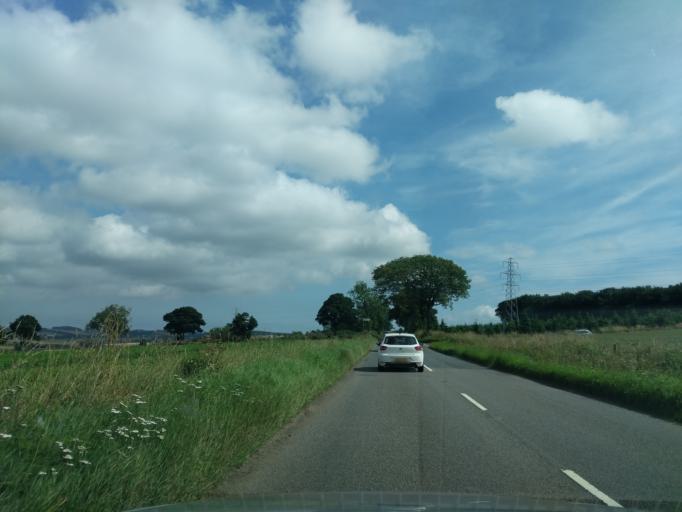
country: GB
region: Scotland
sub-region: Angus
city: Muirhead
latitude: 56.5021
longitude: -3.1127
